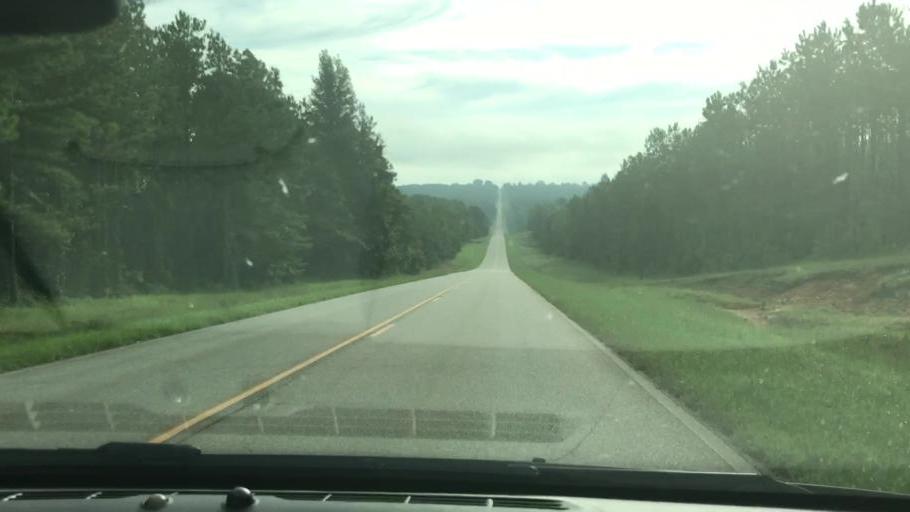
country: US
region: Georgia
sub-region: Quitman County
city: Georgetown
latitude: 31.9757
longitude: -84.9696
